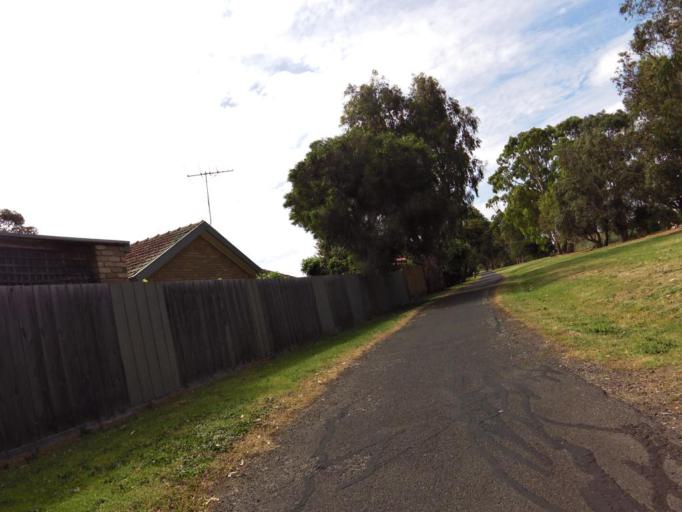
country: AU
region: Victoria
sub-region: Frankston
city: Seaford
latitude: -38.0966
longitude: 145.1350
